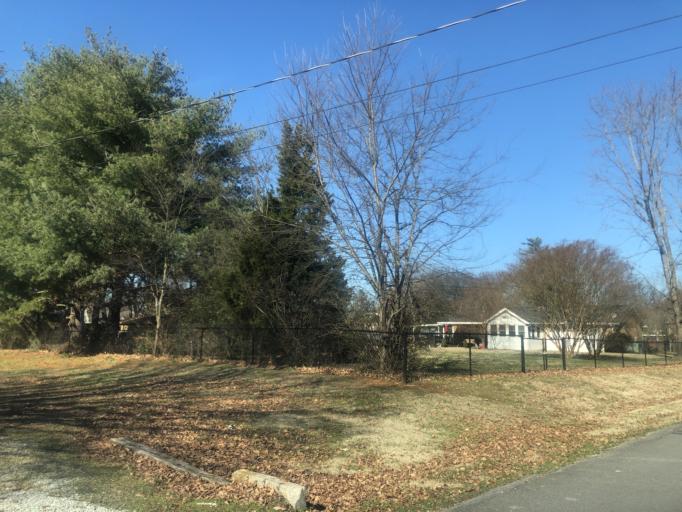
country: US
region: Tennessee
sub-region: Rutherford County
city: Smyrna
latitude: 35.9412
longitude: -86.5308
